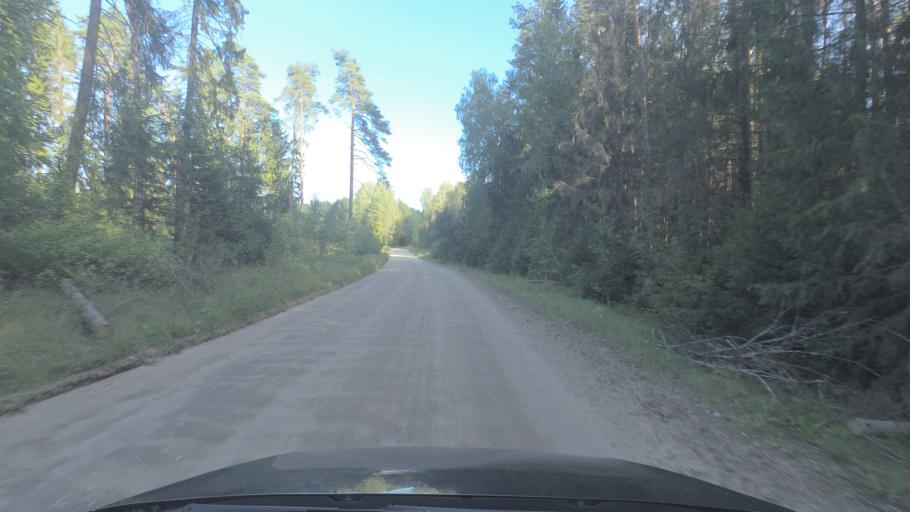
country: LT
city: Svencioneliai
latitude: 55.1642
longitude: 25.8434
